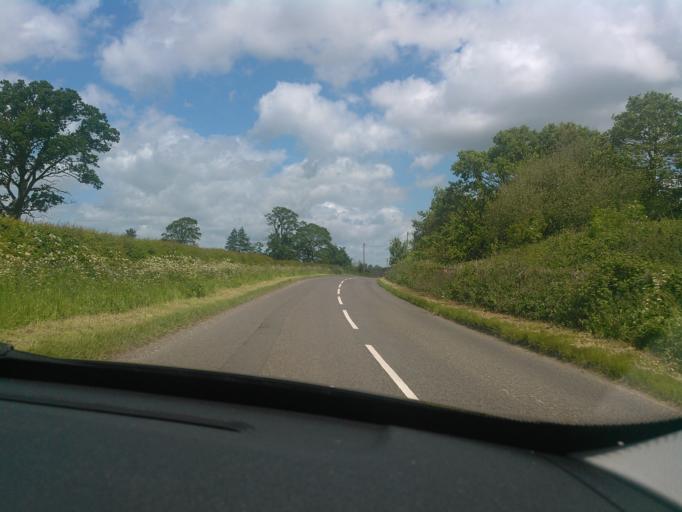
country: GB
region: England
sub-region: Shropshire
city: Prees
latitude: 52.8714
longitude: -2.6640
